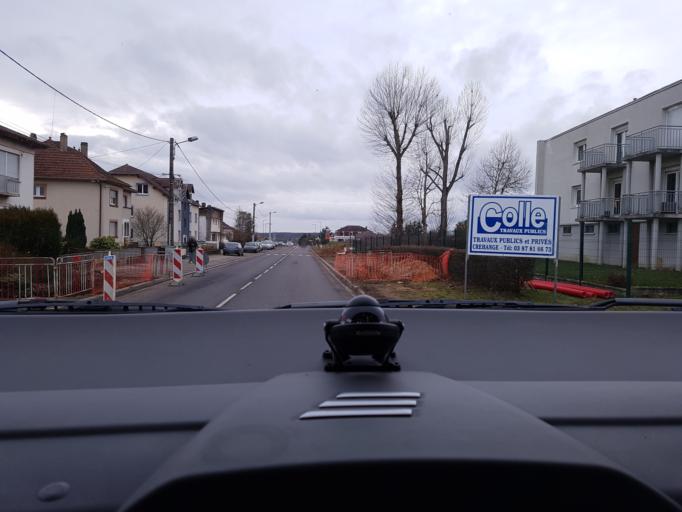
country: FR
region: Lorraine
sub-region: Departement de la Moselle
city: Faulquemont
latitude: 49.0484
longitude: 6.5954
